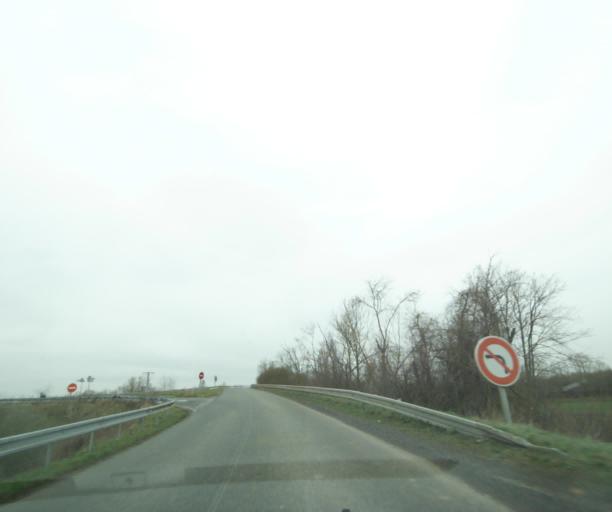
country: FR
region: Nord-Pas-de-Calais
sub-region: Departement du Nord
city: Crespin
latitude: 50.4347
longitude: 3.6618
